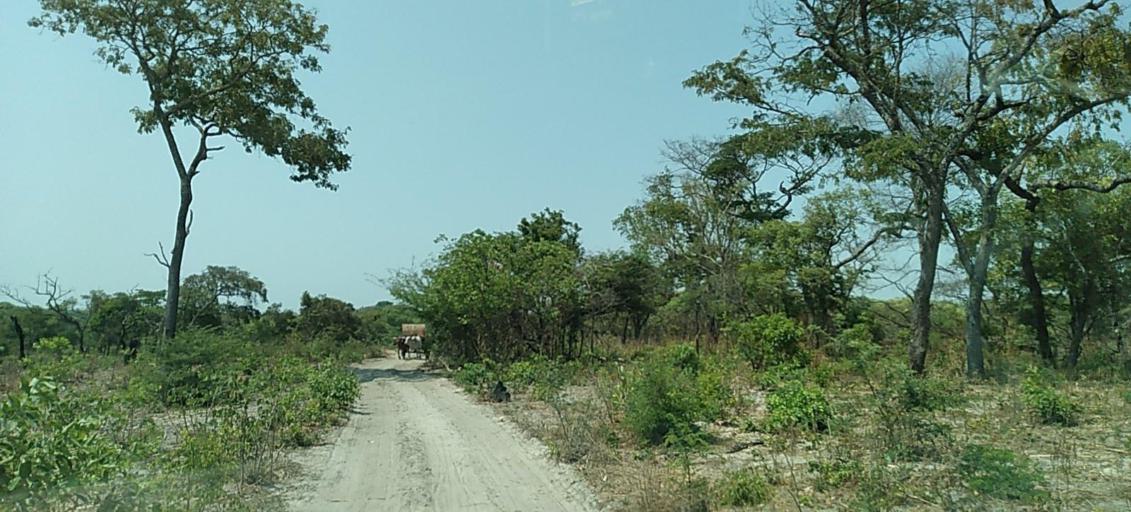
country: ZM
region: Copperbelt
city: Mpongwe
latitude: -13.8425
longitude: 28.0594
